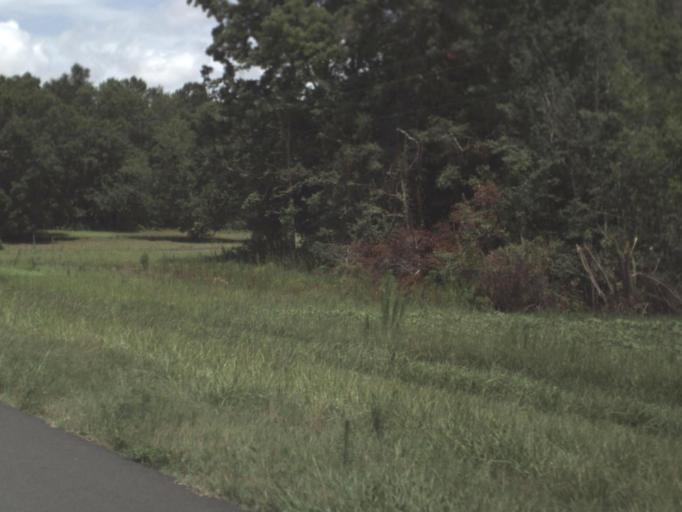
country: US
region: Florida
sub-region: Jefferson County
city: Monticello
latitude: 30.4721
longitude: -83.6567
